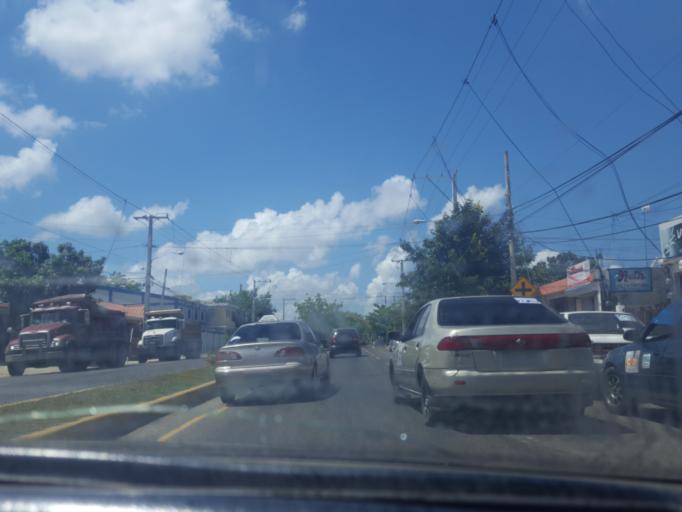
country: DO
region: Santiago
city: Santiago de los Caballeros
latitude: 19.4946
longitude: -70.7033
